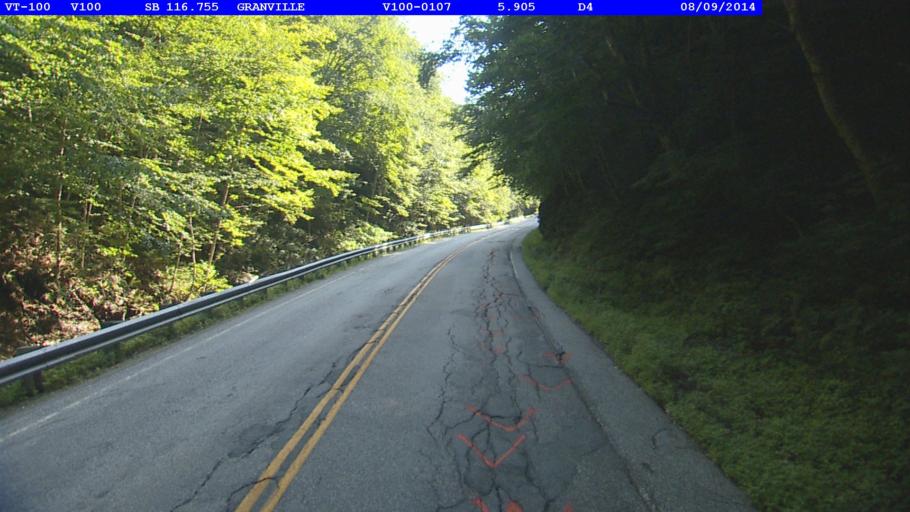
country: US
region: Vermont
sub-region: Orange County
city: Randolph
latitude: 44.0207
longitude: -72.8450
